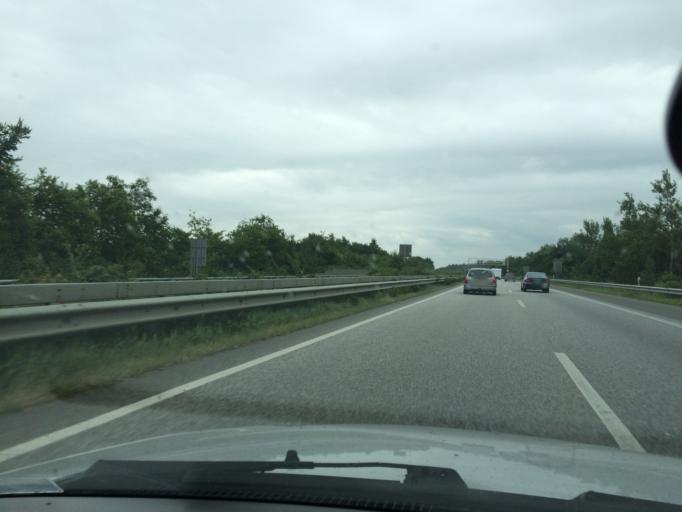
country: DE
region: Schleswig-Holstein
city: Handewitt
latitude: 54.7670
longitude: 9.3518
